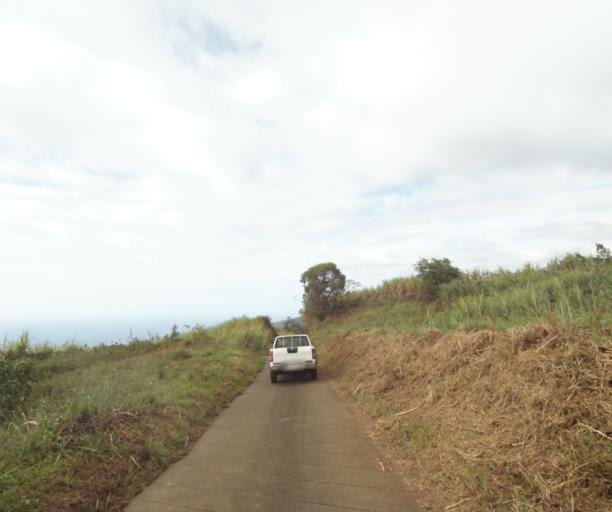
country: RE
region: Reunion
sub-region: Reunion
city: Saint-Paul
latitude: -21.0078
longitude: 55.3487
